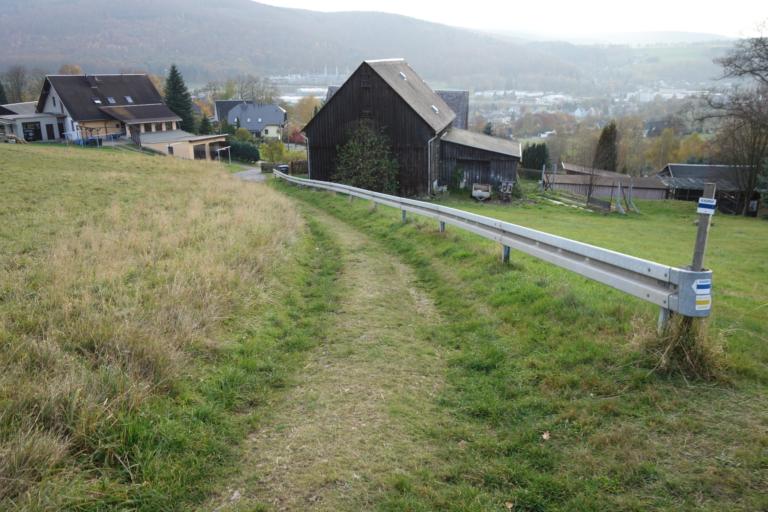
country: DE
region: Saxony
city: Olbernhau
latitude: 50.6546
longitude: 13.3727
